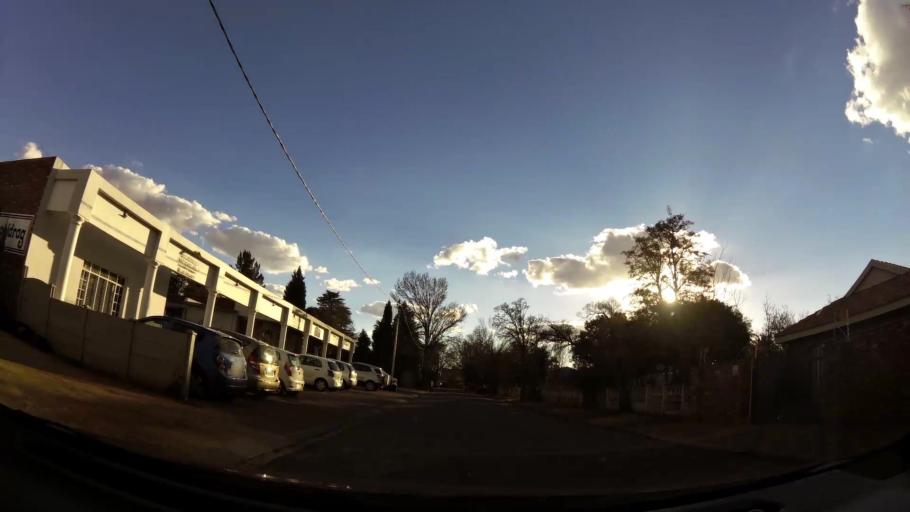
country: ZA
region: North-West
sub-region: Dr Kenneth Kaunda District Municipality
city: Potchefstroom
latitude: -26.7085
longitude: 27.1013
